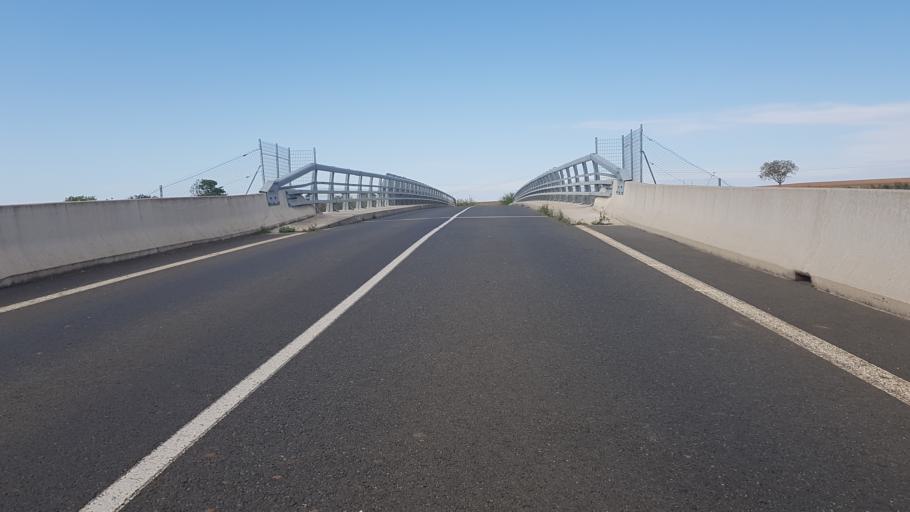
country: FR
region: Poitou-Charentes
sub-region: Departement de la Vienne
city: Chasseneuil-du-Poitou
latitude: 46.6428
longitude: 0.3512
